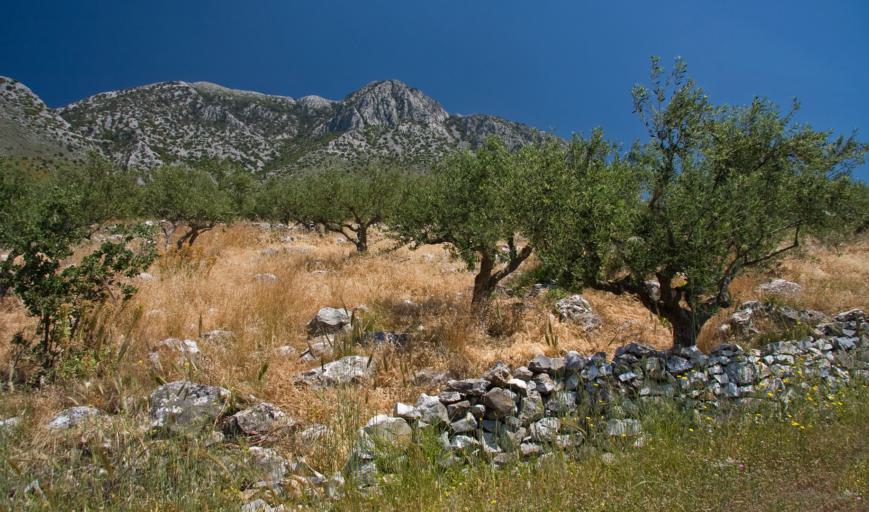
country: GR
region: Peloponnese
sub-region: Nomos Messinias
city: Kardamyli
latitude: 36.7383
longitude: 22.3495
